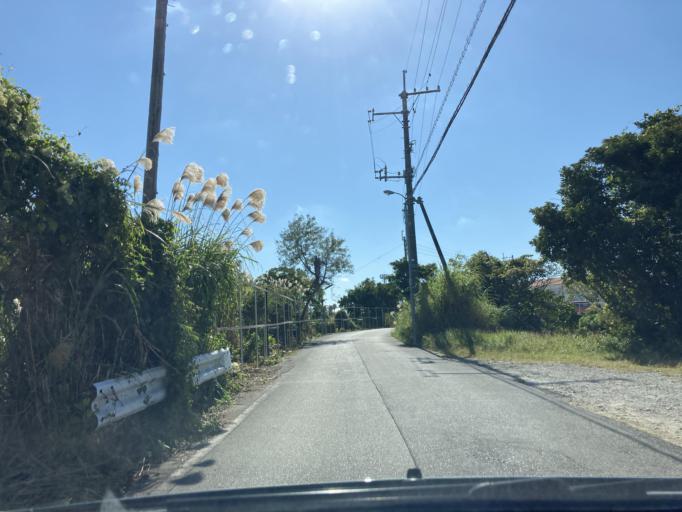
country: JP
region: Okinawa
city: Gushikawa
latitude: 26.3663
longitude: 127.8283
